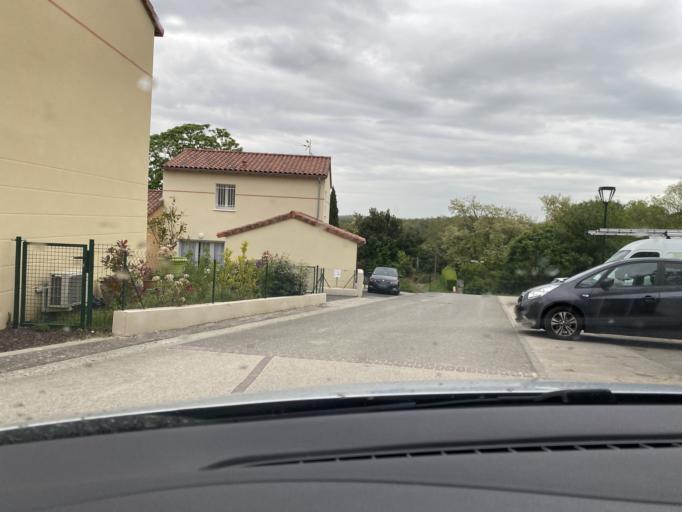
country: FR
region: Midi-Pyrenees
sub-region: Departement de la Haute-Garonne
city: Montgiscard
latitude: 43.4735
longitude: 1.5488
